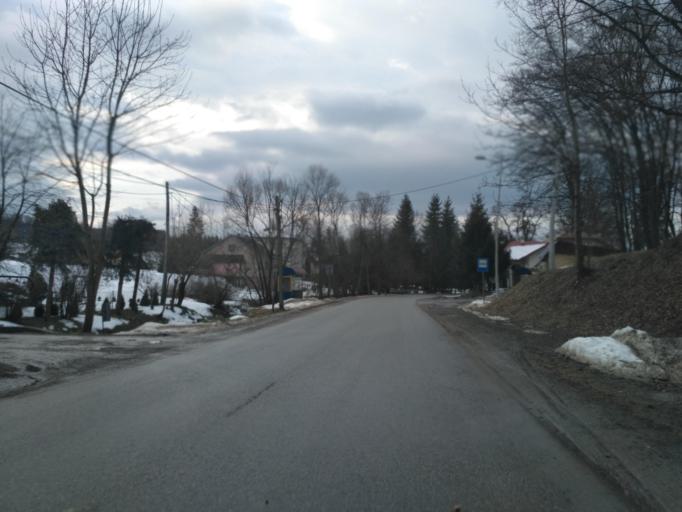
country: PL
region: Subcarpathian Voivodeship
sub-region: Powiat brzozowski
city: Dydnia
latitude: 49.6323
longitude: 22.1677
